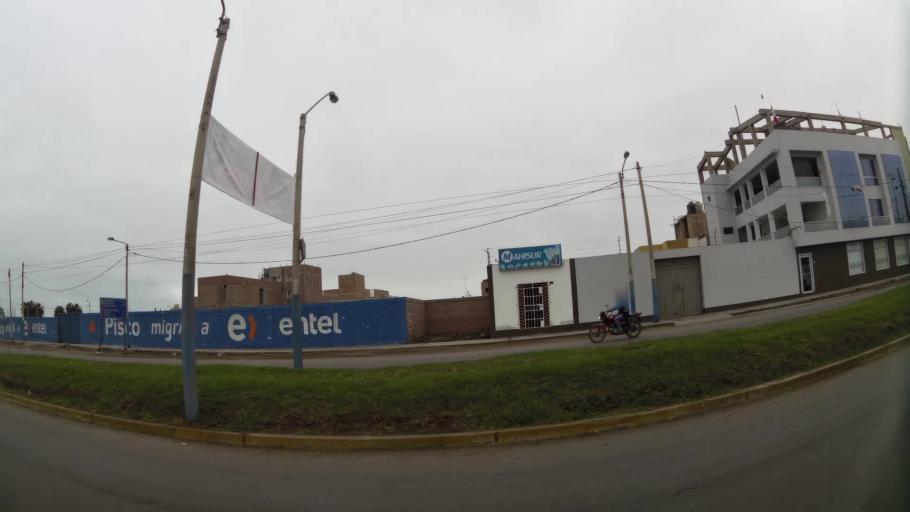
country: PE
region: Ica
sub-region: Provincia de Pisco
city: Pisco
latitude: -13.7163
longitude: -76.2187
